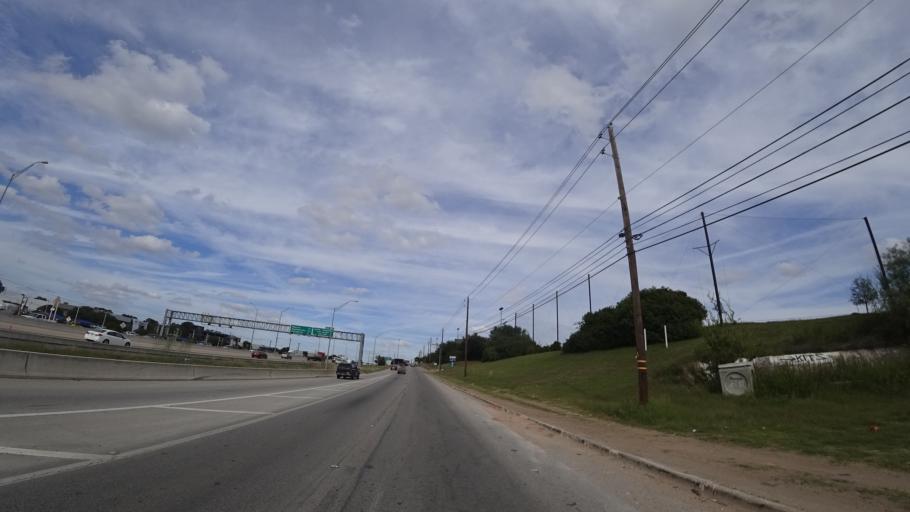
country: US
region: Texas
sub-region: Travis County
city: Austin
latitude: 30.2028
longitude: -97.7600
